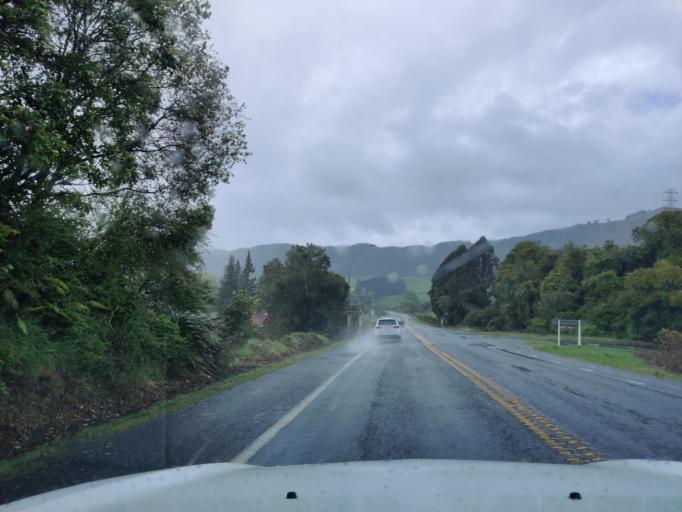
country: NZ
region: Bay of Plenty
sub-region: Rotorua District
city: Rotorua
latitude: -38.0819
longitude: 176.1869
